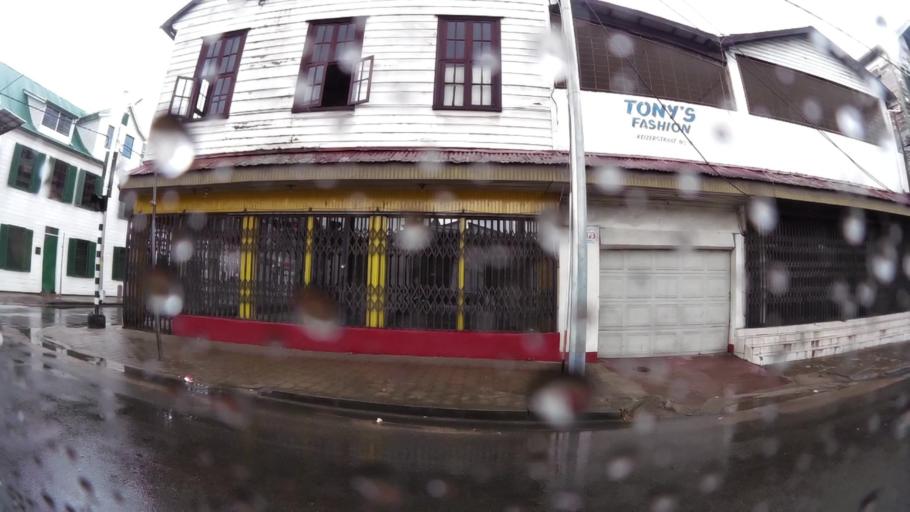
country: SR
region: Paramaribo
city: Paramaribo
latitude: 5.8257
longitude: -55.1551
